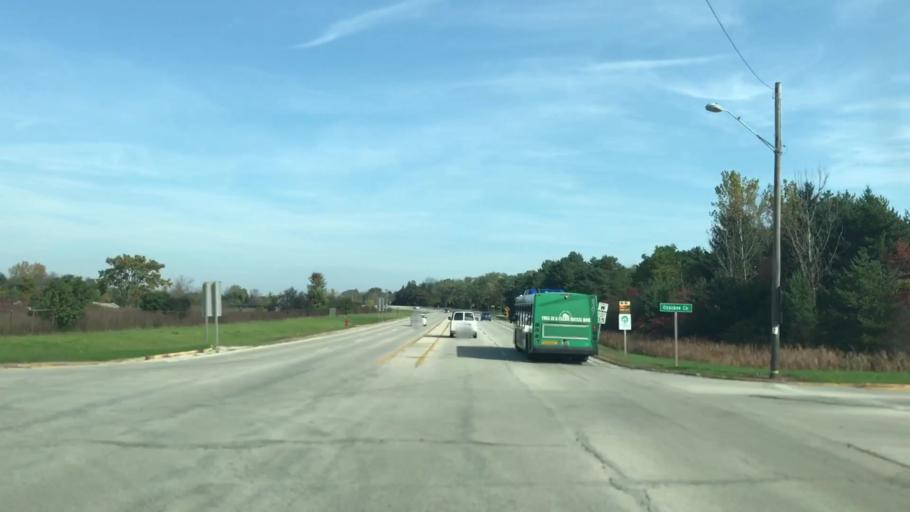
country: US
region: Wisconsin
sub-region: Milwaukee County
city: River Hills
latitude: 43.1921
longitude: -87.9233
